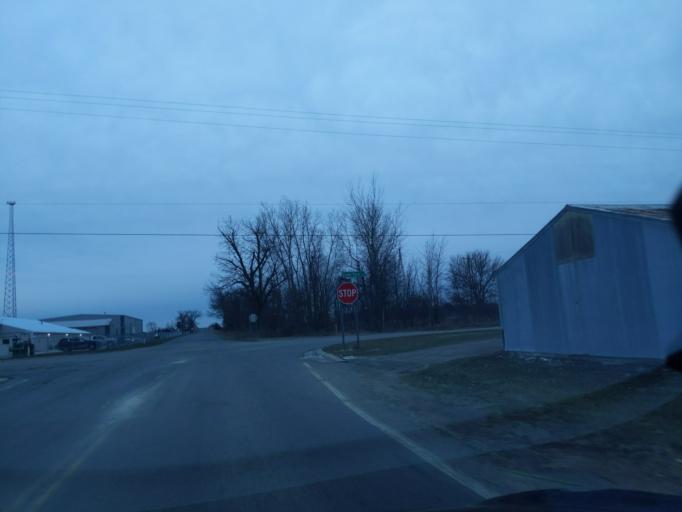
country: US
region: Michigan
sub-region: Ionia County
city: Portland
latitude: 42.8718
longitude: -84.9560
